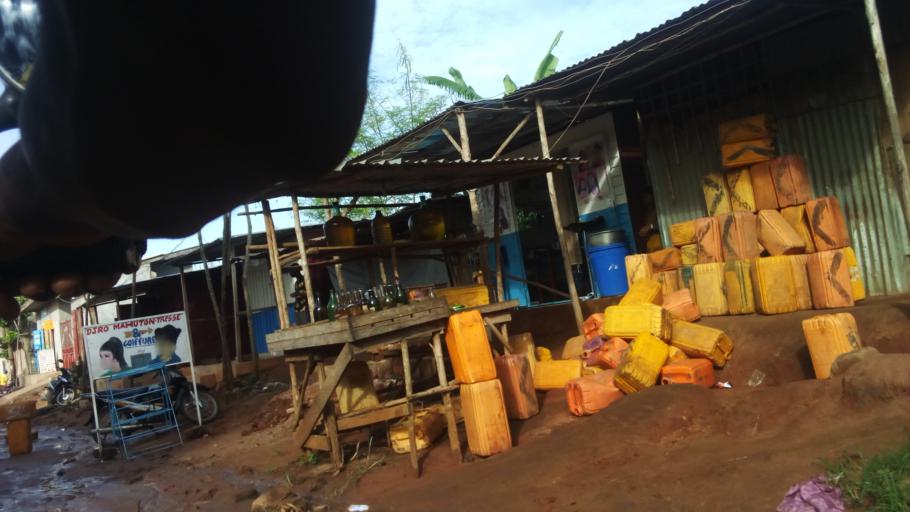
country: BJ
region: Atlantique
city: Abomey-Calavi
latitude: 6.4272
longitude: 2.3395
